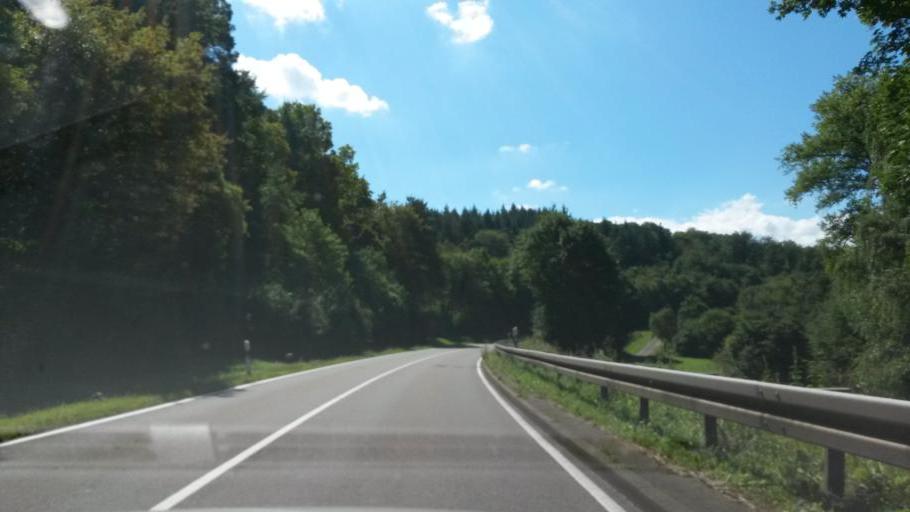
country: DE
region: Baden-Wuerttemberg
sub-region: Karlsruhe Region
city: Ispringen
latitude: 48.9241
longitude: 8.6372
